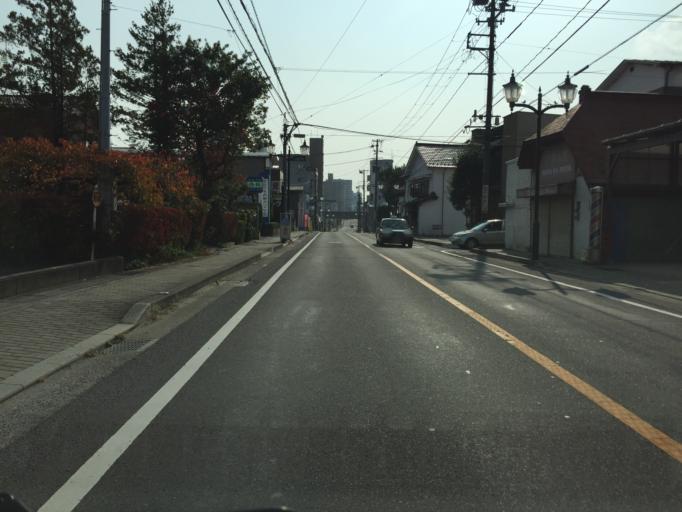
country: JP
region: Fukushima
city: Koriyama
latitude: 37.4082
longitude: 140.3898
